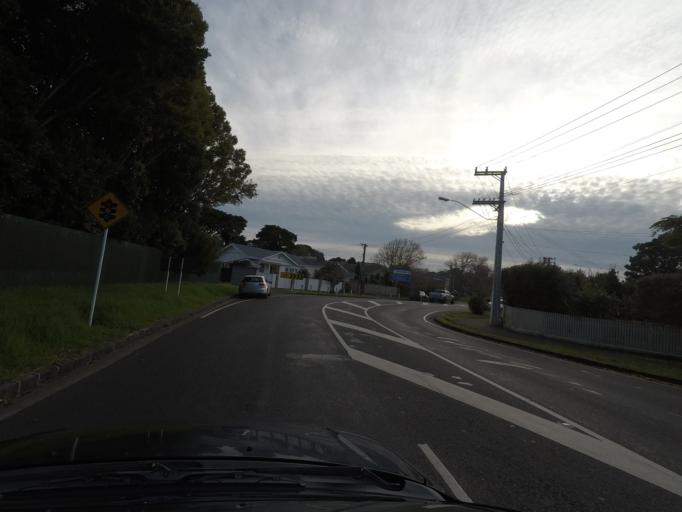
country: NZ
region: Auckland
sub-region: Auckland
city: Auckland
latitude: -36.8862
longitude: 174.8041
